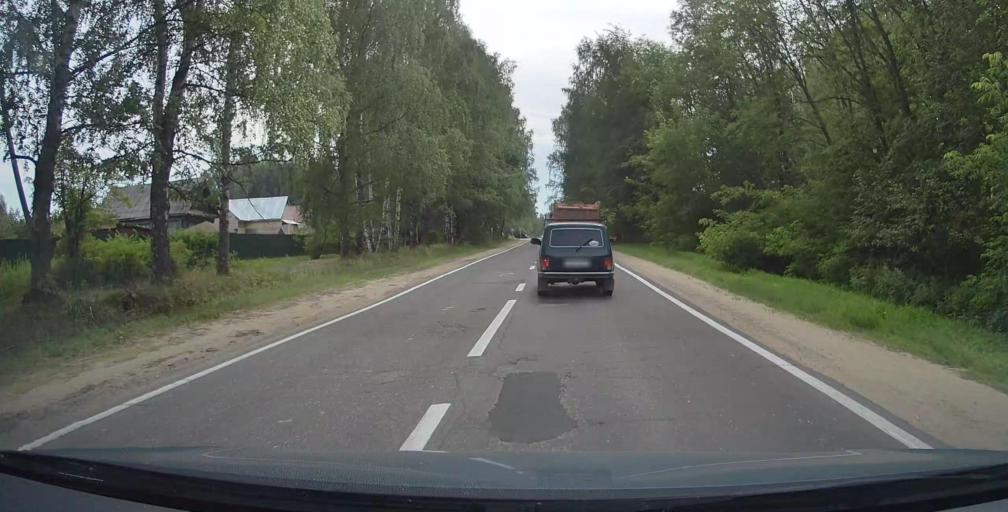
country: RU
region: Jaroslavl
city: Rybinsk
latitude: 58.0008
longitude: 38.7584
